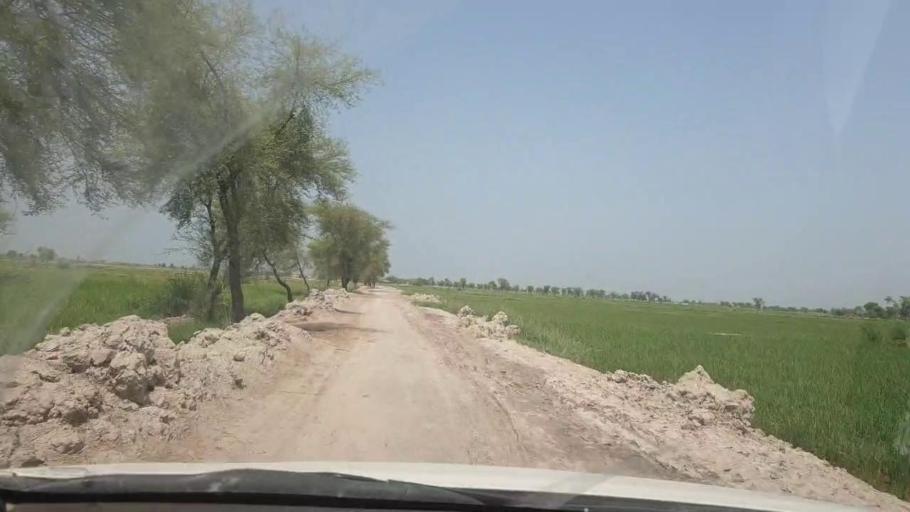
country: PK
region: Sindh
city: Lakhi
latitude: 27.8714
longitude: 68.7326
